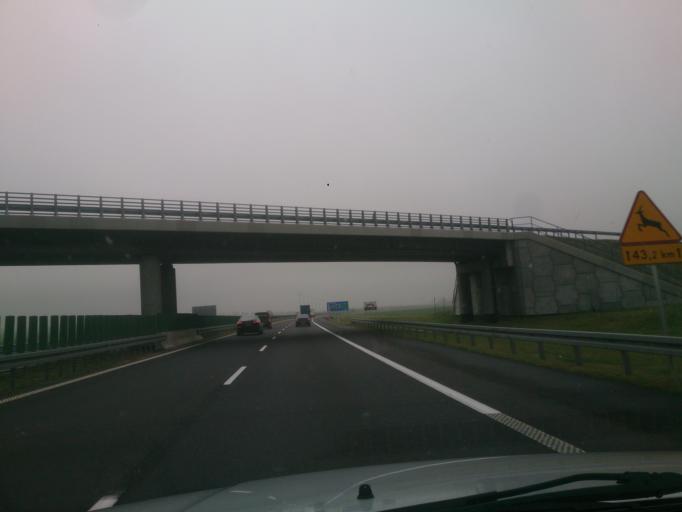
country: PL
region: Pomeranian Voivodeship
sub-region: Powiat starogardzki
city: Smetowo Graniczne
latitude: 53.7250
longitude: 18.6286
